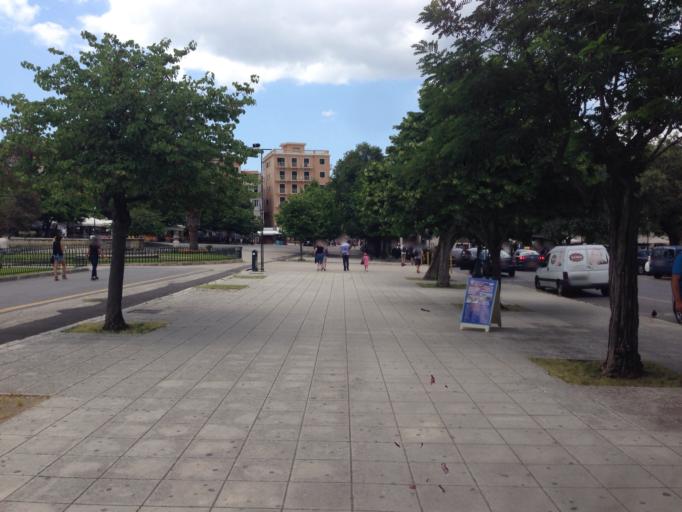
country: GR
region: Ionian Islands
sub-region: Nomos Kerkyras
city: Kerkyra
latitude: 39.6234
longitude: 19.9251
